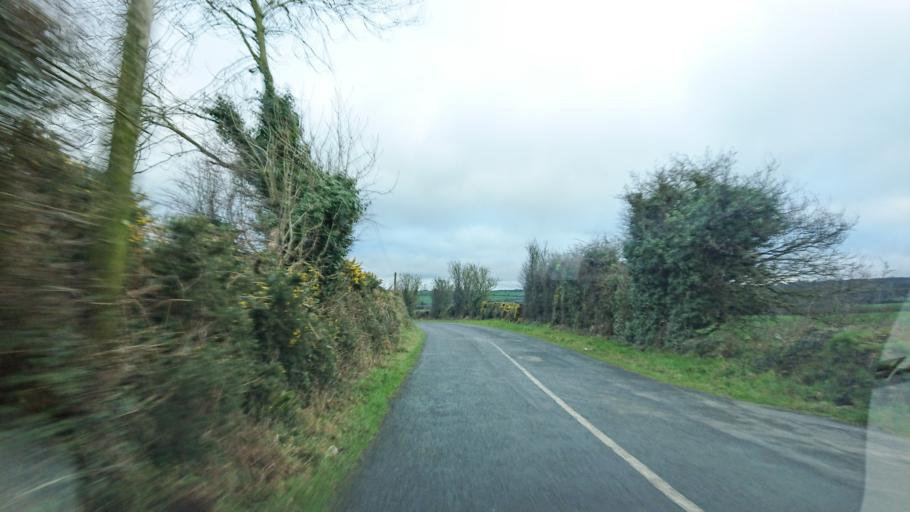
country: IE
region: Munster
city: Carrick-on-Suir
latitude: 52.2484
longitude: -7.4149
